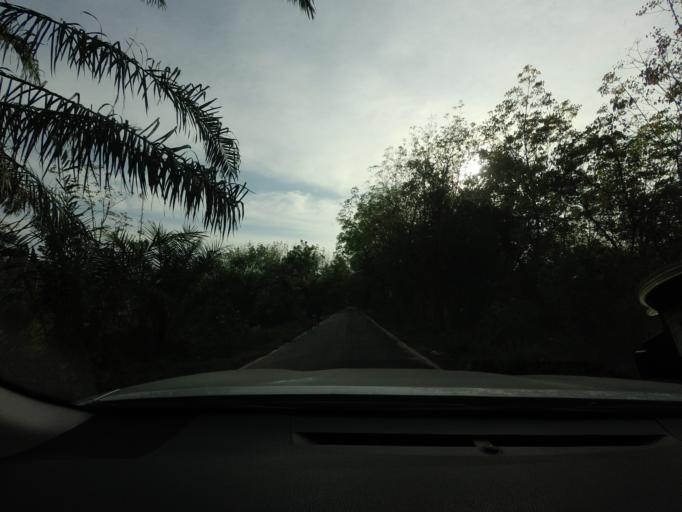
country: TH
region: Narathiwat
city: Ra-ngae
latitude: 6.3038
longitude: 101.7740
